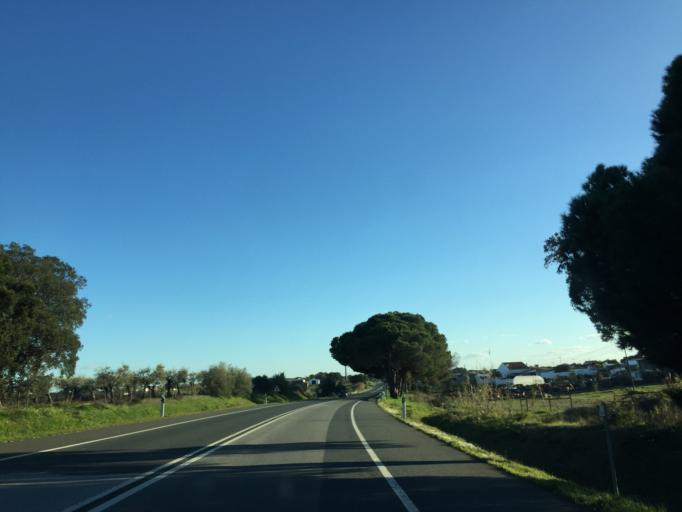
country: PT
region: Setubal
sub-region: Grandola
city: Grandola
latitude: 38.0539
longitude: -8.4031
